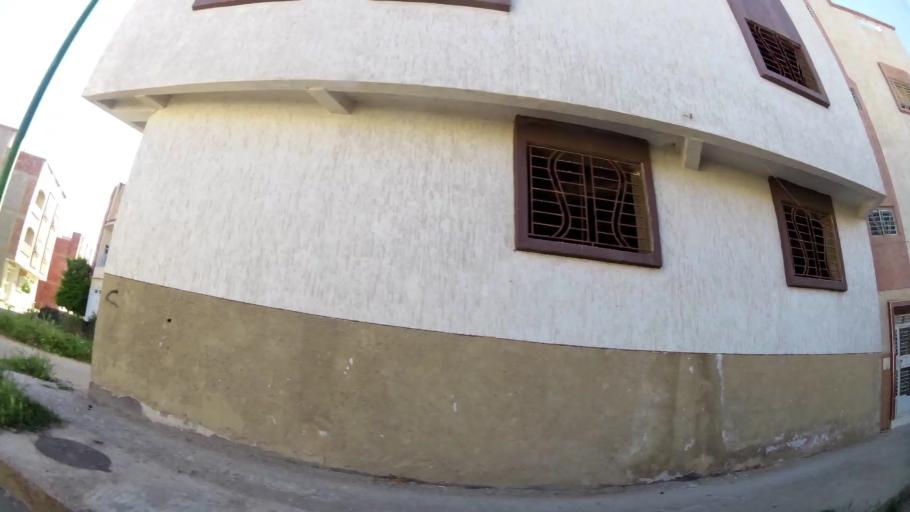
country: MA
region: Meknes-Tafilalet
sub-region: Meknes
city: Meknes
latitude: 33.8770
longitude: -5.5764
